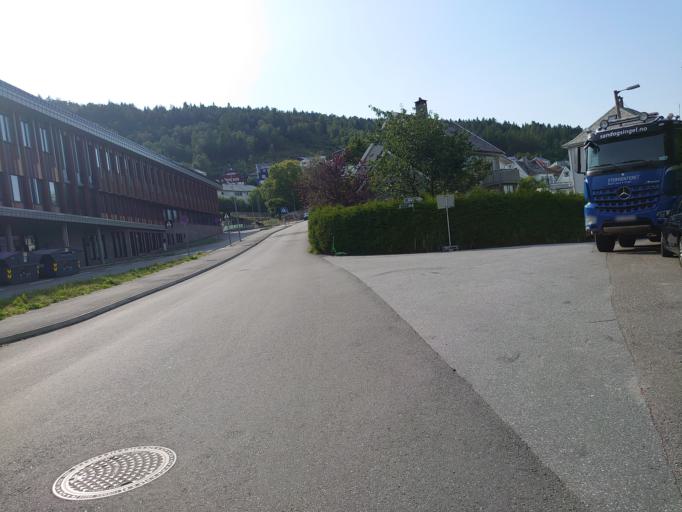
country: NO
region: Hordaland
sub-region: Bergen
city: Bergen
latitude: 60.3824
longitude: 5.3030
